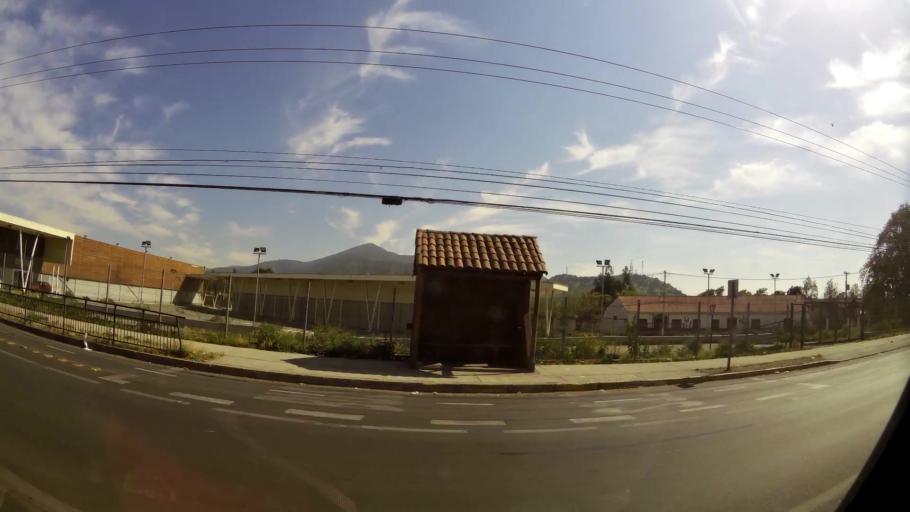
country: CL
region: Santiago Metropolitan
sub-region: Provincia de Talagante
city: Talagante
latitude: -33.6698
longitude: -70.9399
